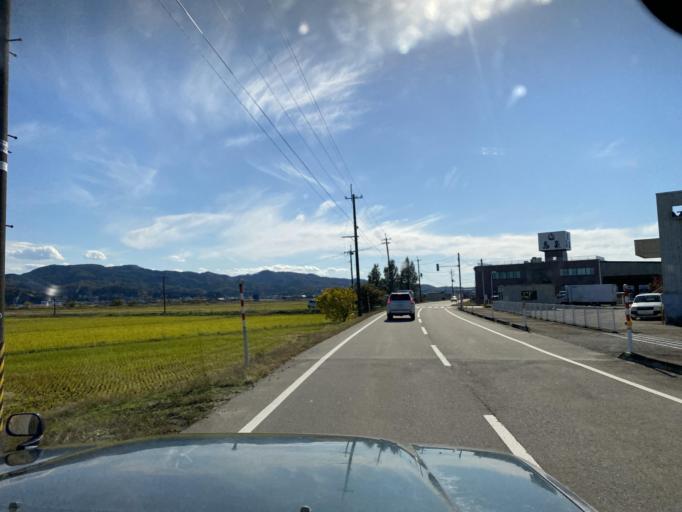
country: JP
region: Niigata
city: Niitsu-honcho
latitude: 37.7592
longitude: 139.0872
